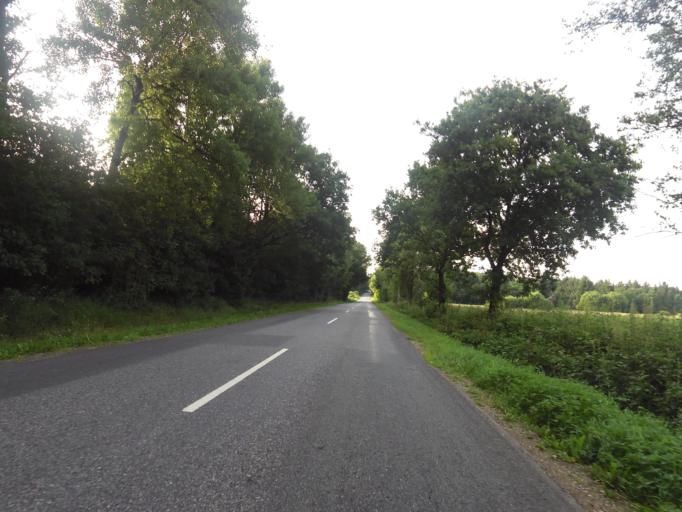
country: DK
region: South Denmark
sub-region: Tonder Kommune
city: Sherrebek
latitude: 55.1965
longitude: 8.8935
